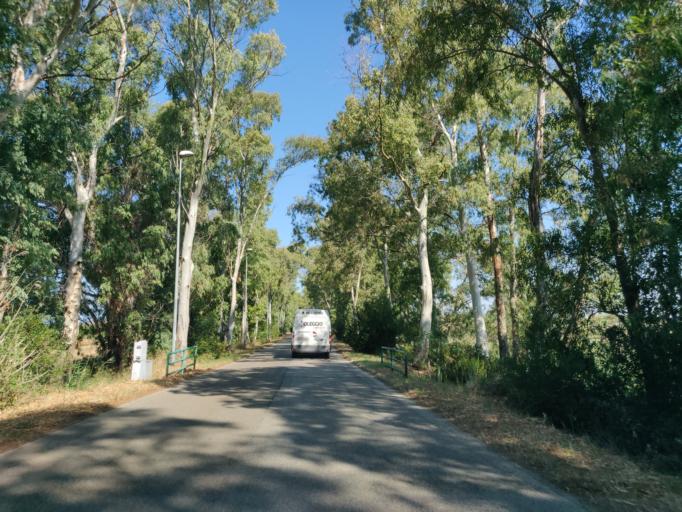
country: IT
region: Latium
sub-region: Citta metropolitana di Roma Capitale
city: Aurelia
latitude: 42.1554
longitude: 11.7547
